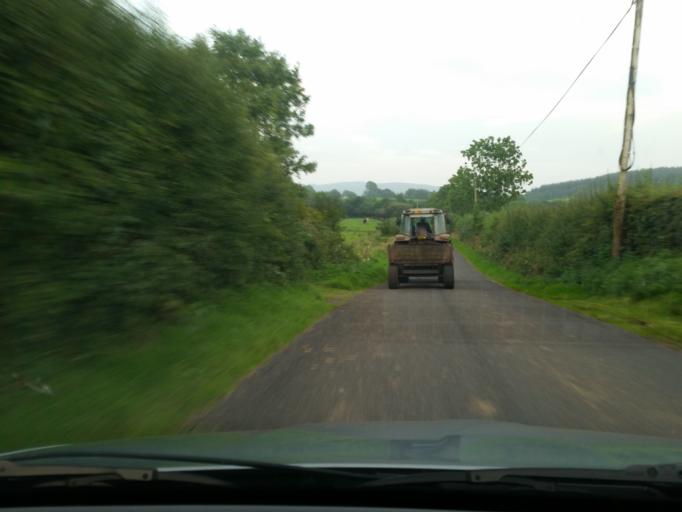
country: GB
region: Northern Ireland
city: Fivemiletown
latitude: 54.3686
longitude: -7.2896
